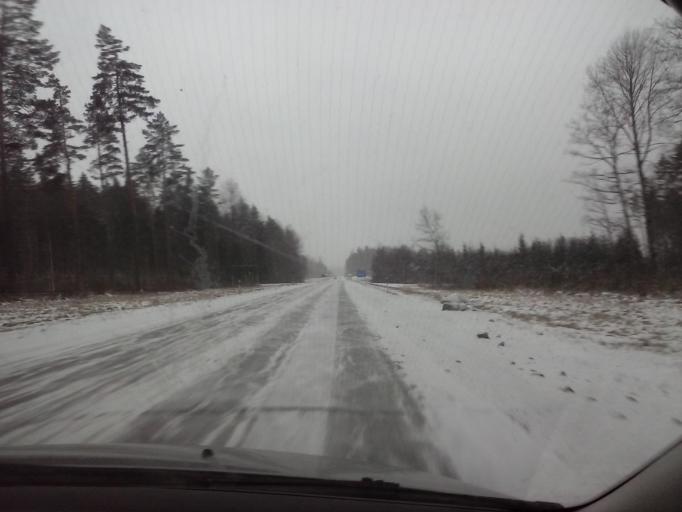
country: EE
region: Valgamaa
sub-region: Valga linn
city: Valga
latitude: 57.8613
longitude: 26.1424
